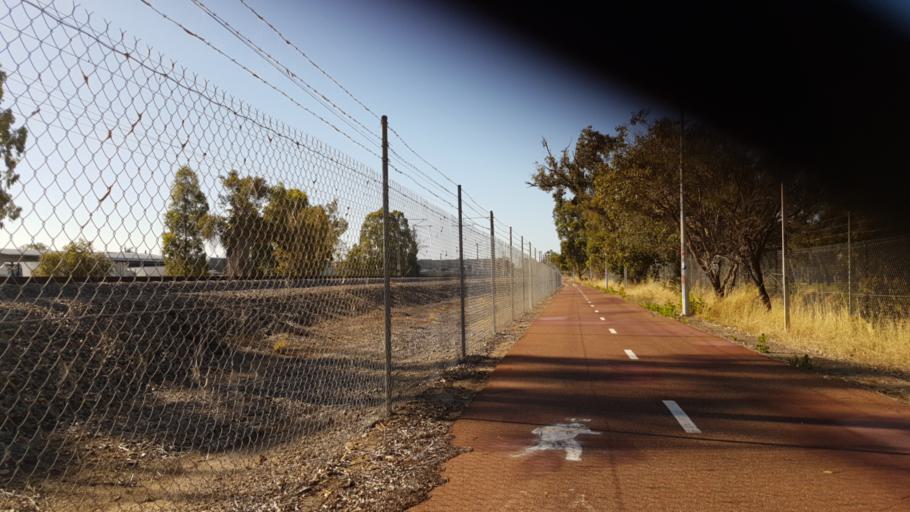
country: AU
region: Western Australia
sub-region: Gosnells
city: Kenwick
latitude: -32.0419
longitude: 115.9746
